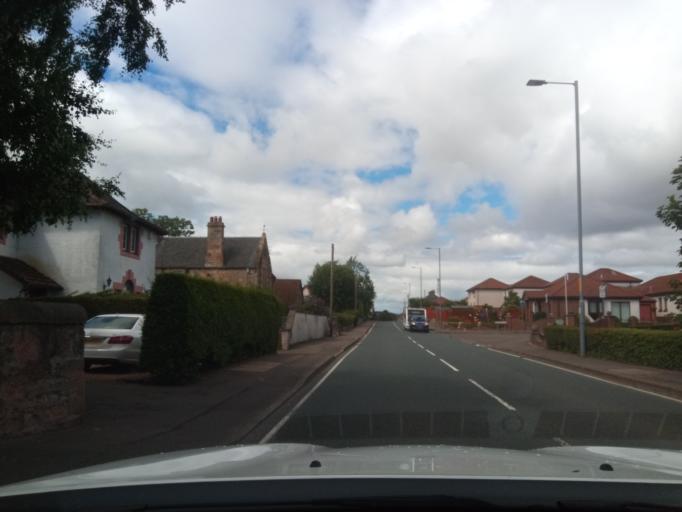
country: GB
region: Scotland
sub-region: Fife
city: Kincardine
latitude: 56.0678
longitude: -3.7106
